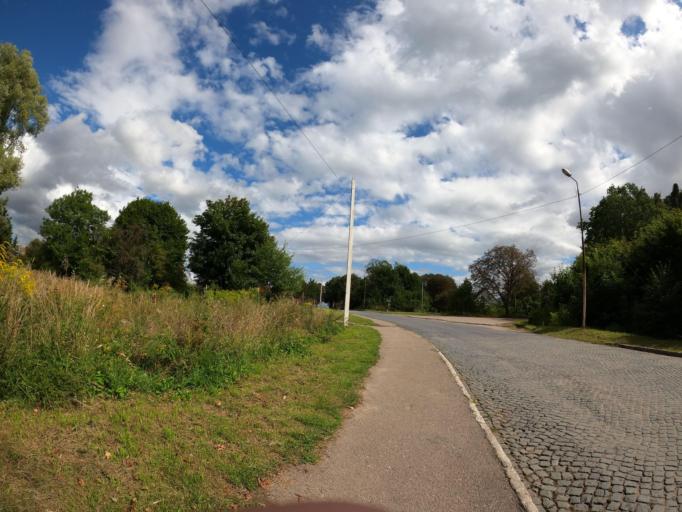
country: RU
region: Kaliningrad
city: Zheleznodorozhnyy
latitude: 54.3537
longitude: 21.3175
